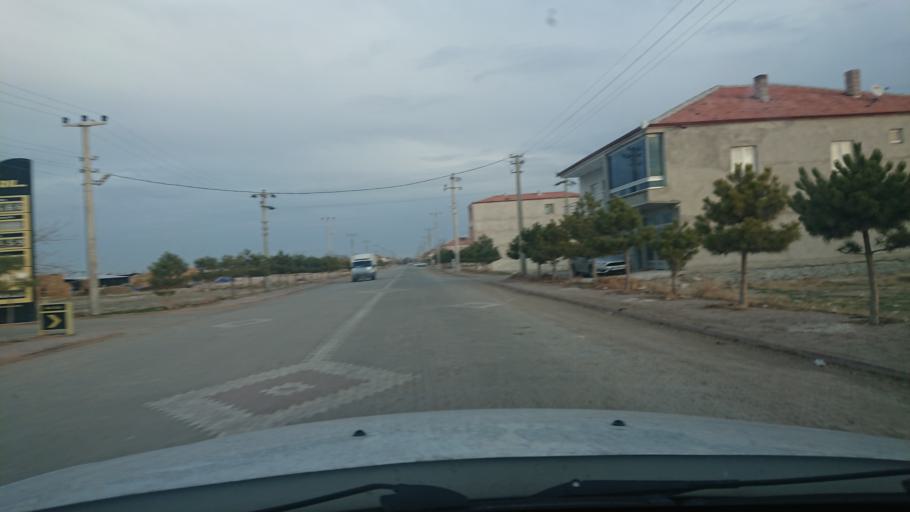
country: TR
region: Aksaray
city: Yesilova
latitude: 38.3356
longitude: 33.7513
